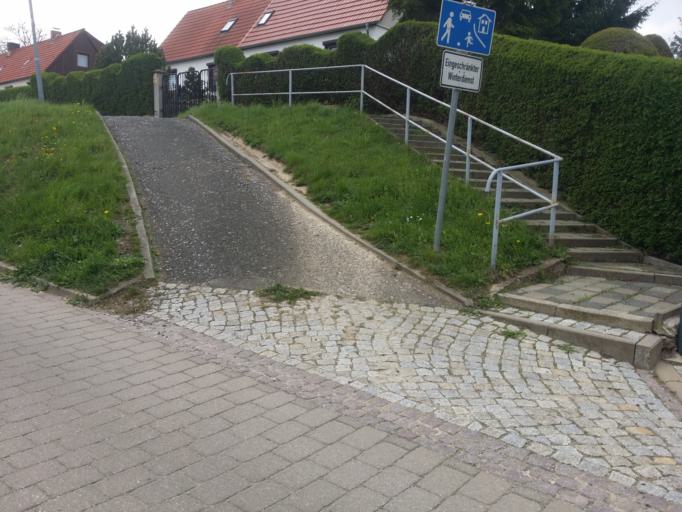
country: DE
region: Saxony-Anhalt
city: Neinstedt
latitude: 51.7467
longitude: 11.0860
